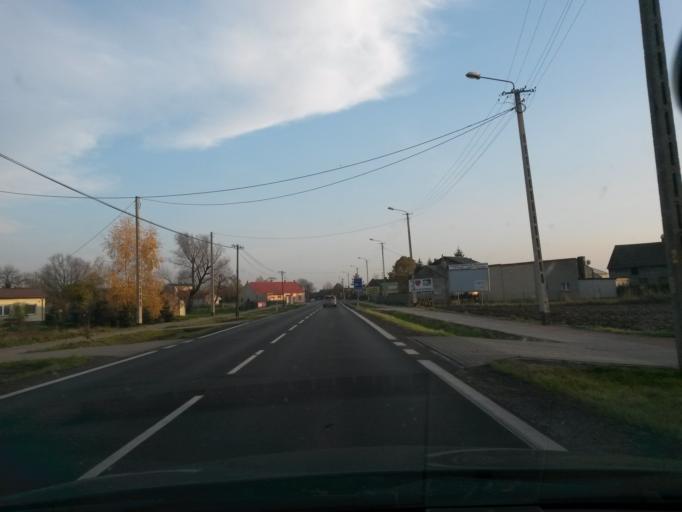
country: PL
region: Lodz Voivodeship
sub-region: Powiat wielunski
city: Wielun
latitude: 51.2331
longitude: 18.5389
